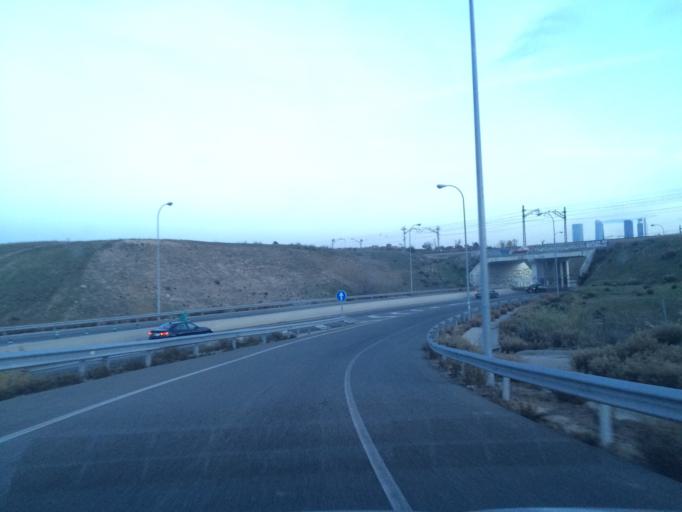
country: ES
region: Madrid
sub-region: Provincia de Madrid
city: Fuencarral-El Pardo
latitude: 40.4997
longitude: -3.7214
